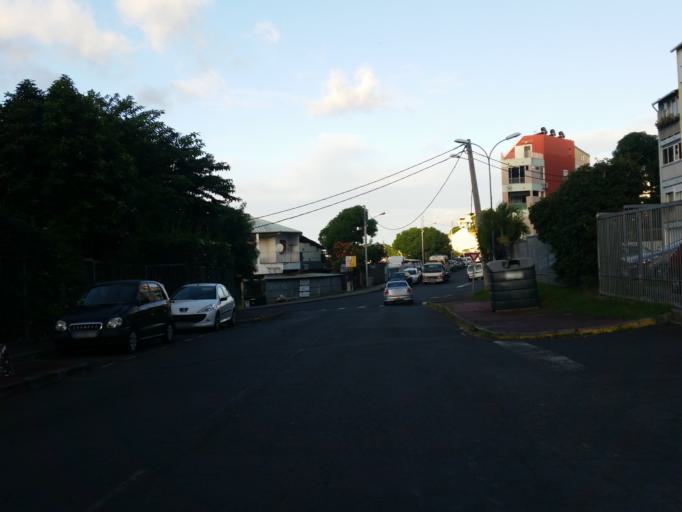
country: RE
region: Reunion
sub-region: Reunion
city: Saint-Denis
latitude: -20.8913
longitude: 55.4472
